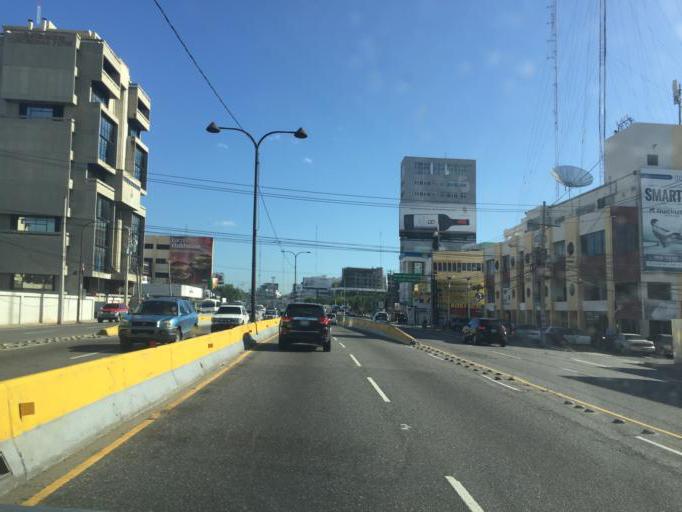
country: DO
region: Nacional
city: La Julia
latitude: 18.4678
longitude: -69.9258
